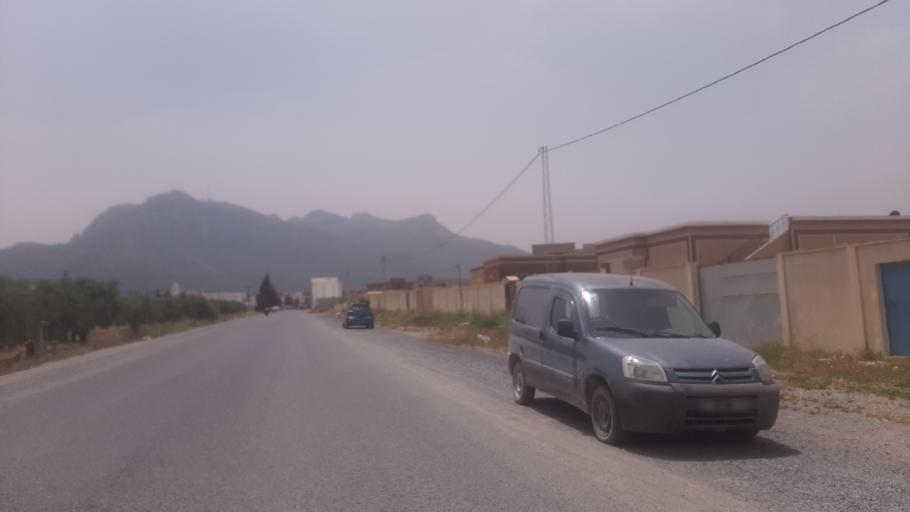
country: TN
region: Zaghwan
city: Zaghouan
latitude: 36.4173
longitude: 10.1363
